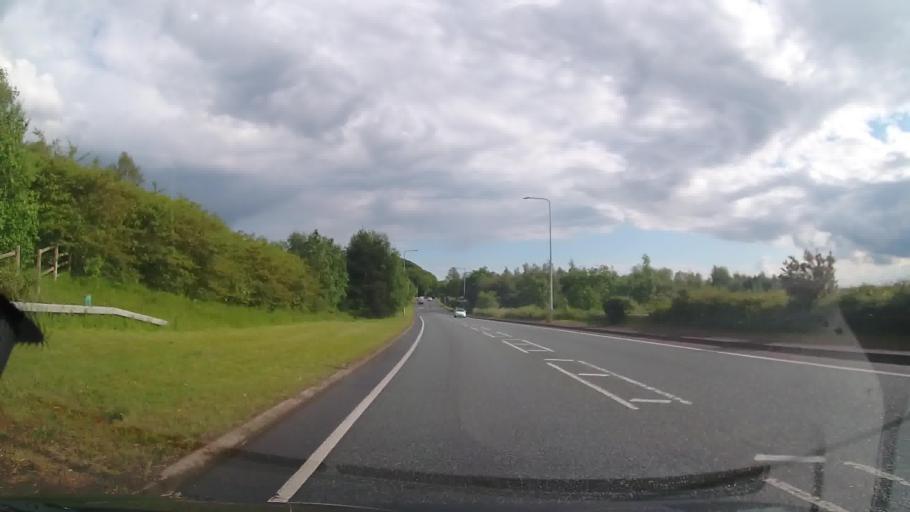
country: GB
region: England
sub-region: Shropshire
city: Hadley
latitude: 52.6674
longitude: -2.4908
